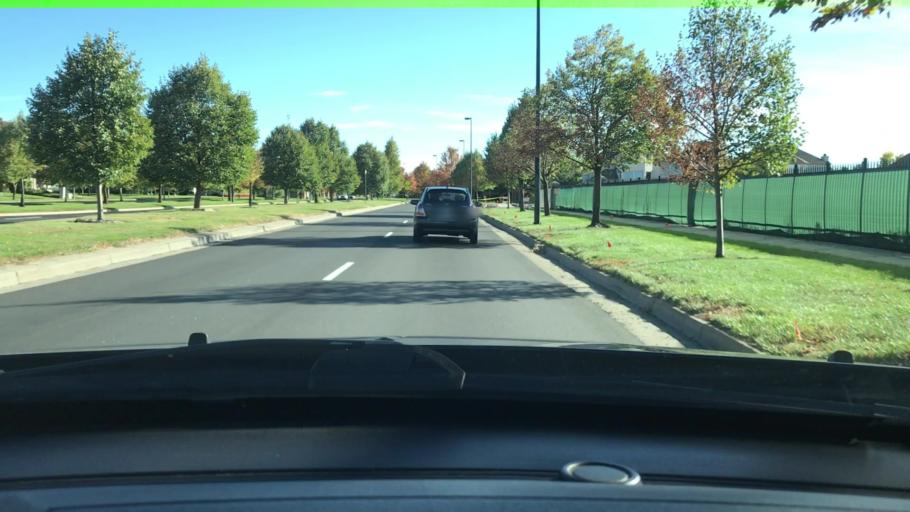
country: US
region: Colorado
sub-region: Arapahoe County
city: Glendale
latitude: 39.7160
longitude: -104.9038
